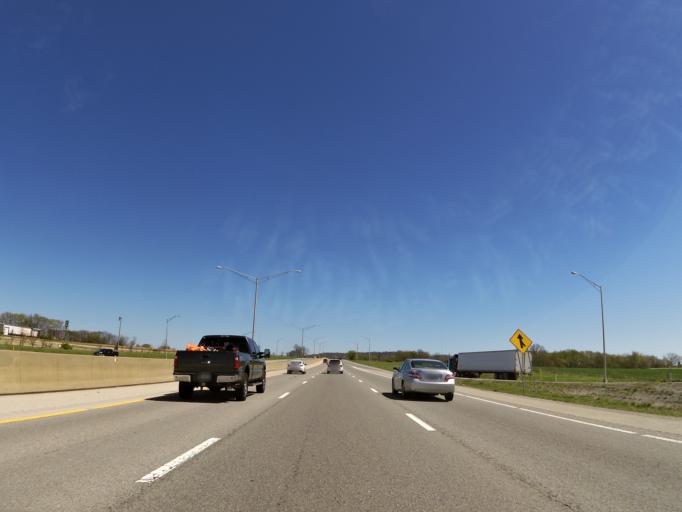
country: US
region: Kentucky
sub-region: Edmonson County
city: Brownsville
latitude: 37.0419
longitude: -86.2085
